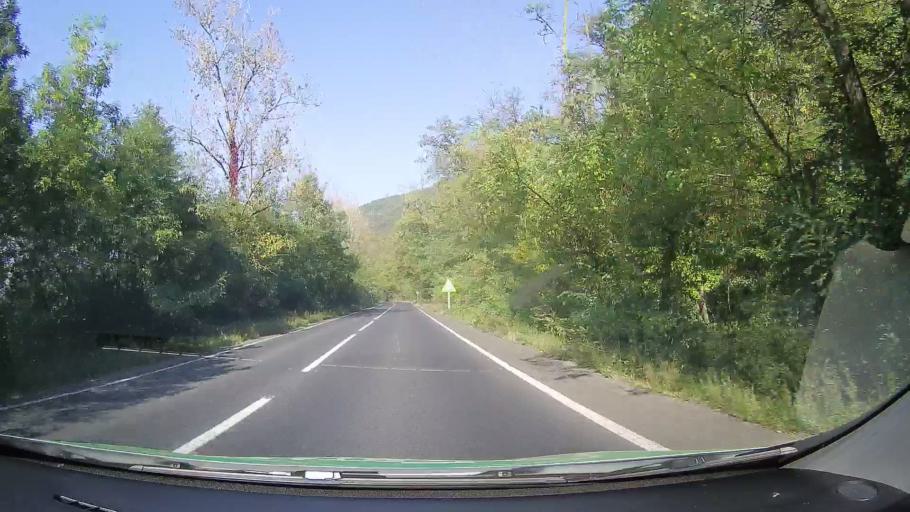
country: RO
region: Arad
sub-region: Comuna Savarsin
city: Savarsin
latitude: 46.0063
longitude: 22.2746
